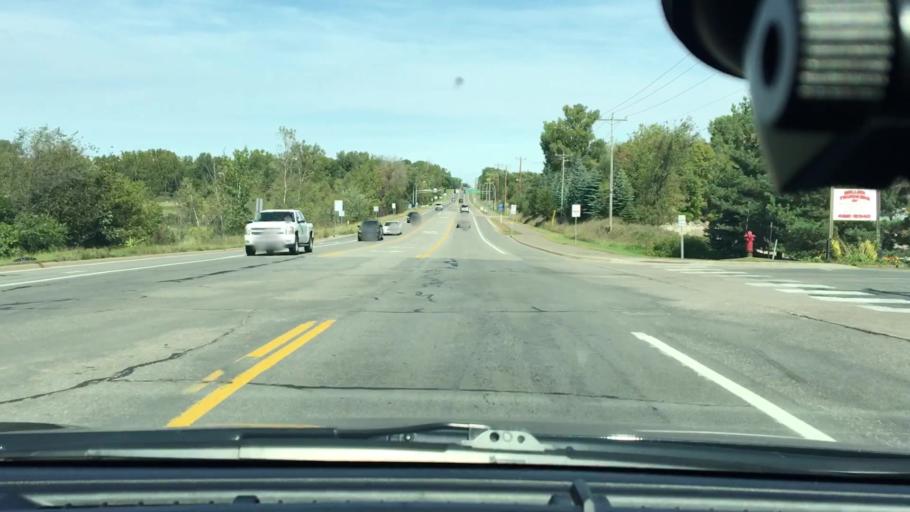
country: US
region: Minnesota
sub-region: Wright County
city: Hanover
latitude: 45.1589
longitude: -93.6660
